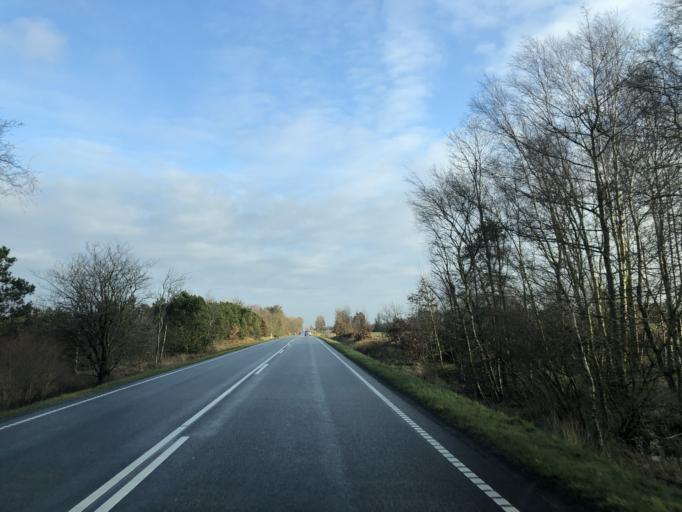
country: DK
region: Central Jutland
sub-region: Holstebro Kommune
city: Ulfborg
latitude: 56.3238
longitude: 8.4601
